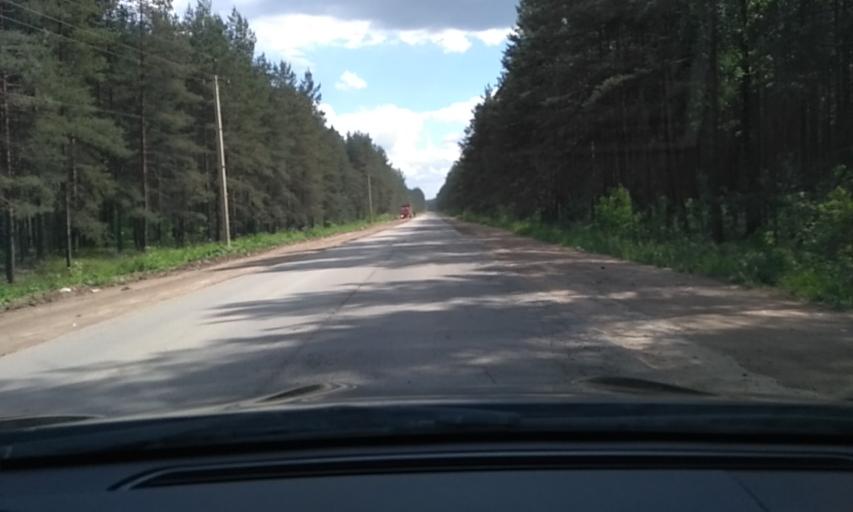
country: RU
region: Leningrad
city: Imeni Sverdlova
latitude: 59.8522
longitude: 30.6781
